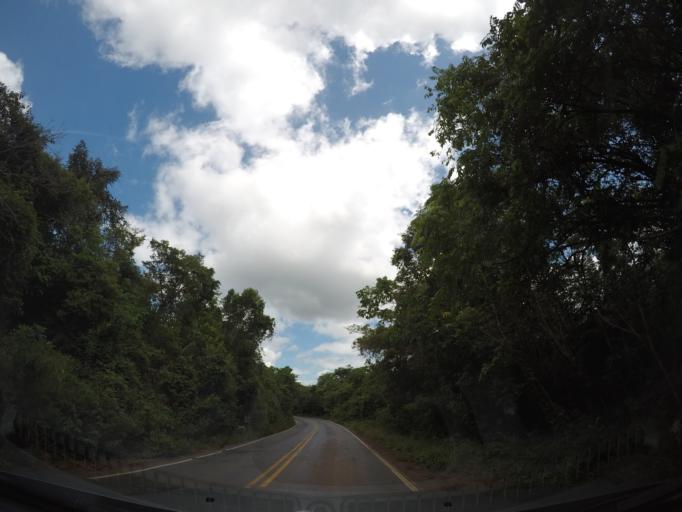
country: BR
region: Bahia
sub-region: Andarai
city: Vera Cruz
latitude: -12.5092
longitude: -41.3614
